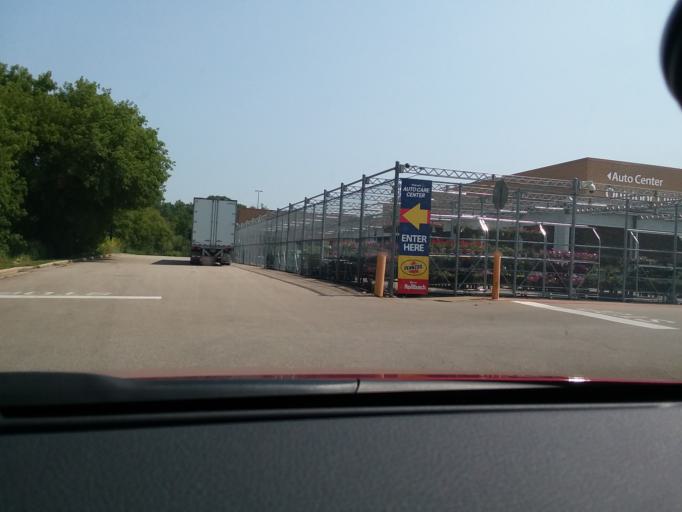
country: US
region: Wisconsin
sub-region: Dane County
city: Monona
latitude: 43.1113
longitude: -89.3142
